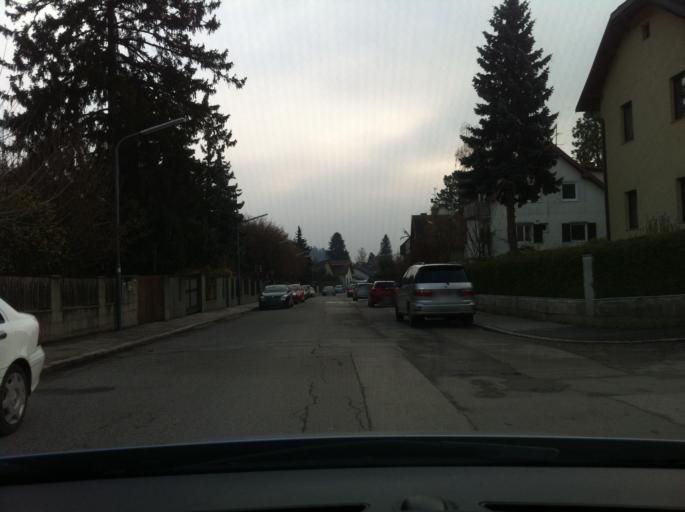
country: AT
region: Lower Austria
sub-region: Politischer Bezirk Wien-Umgebung
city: Purkersdorf
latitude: 48.2236
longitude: 16.2465
